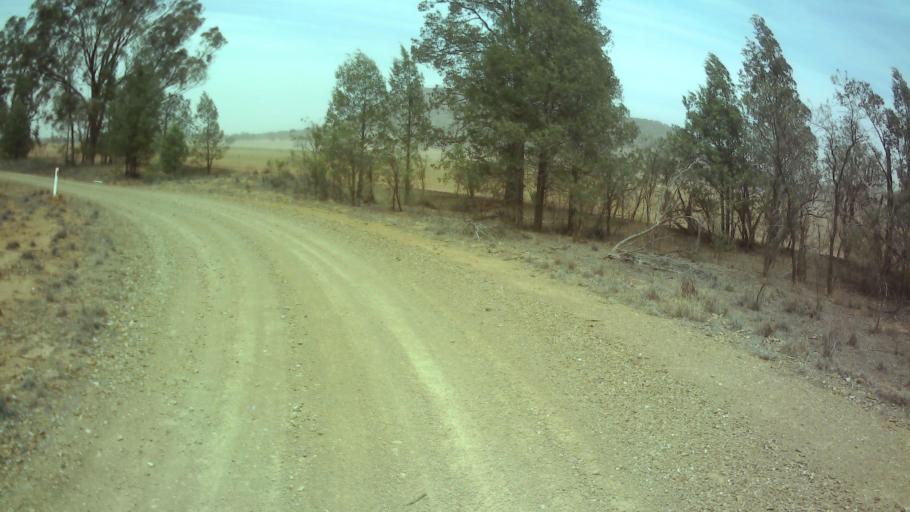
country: AU
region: New South Wales
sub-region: Weddin
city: Grenfell
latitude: -33.7178
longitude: 147.9655
